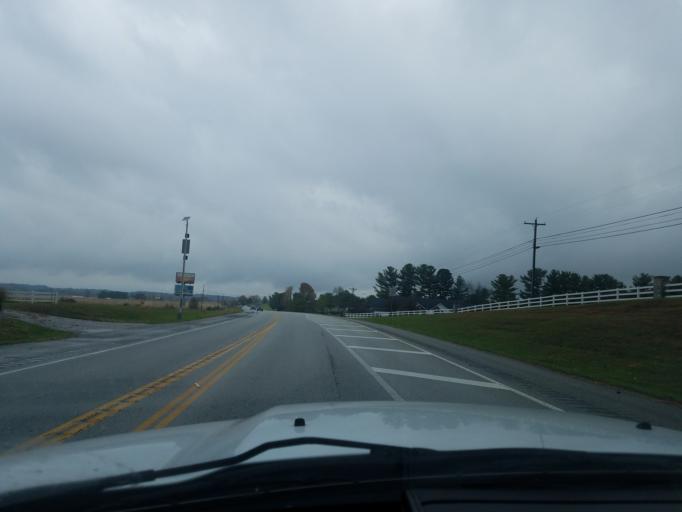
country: US
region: Kentucky
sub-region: Taylor County
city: Campbellsville
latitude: 37.3610
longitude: -85.3812
